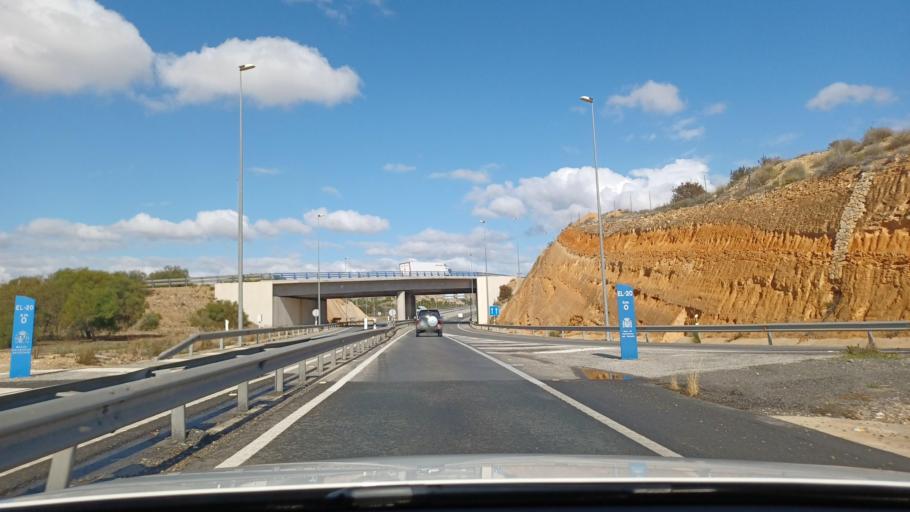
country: ES
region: Valencia
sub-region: Provincia de Alicante
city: Elche
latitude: 38.2995
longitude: -0.6693
